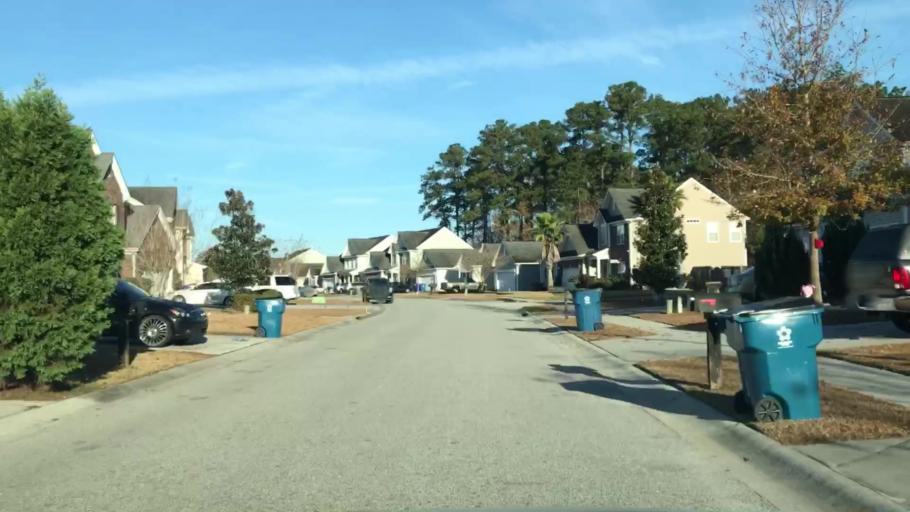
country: US
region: South Carolina
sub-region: Charleston County
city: Lincolnville
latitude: 32.9901
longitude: -80.1452
